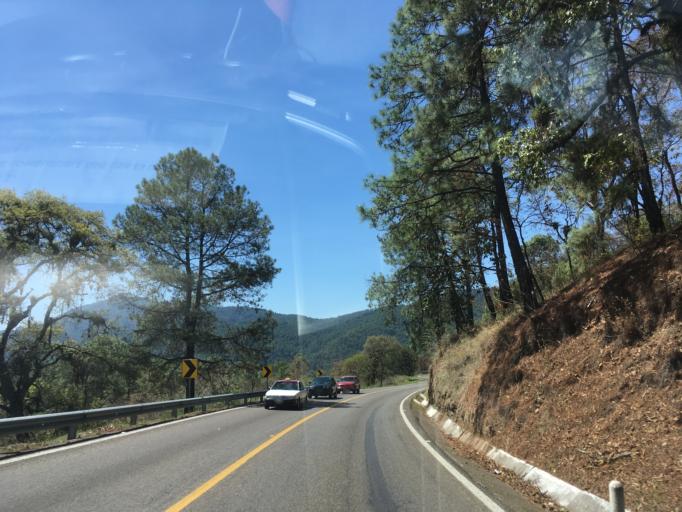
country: MX
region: Michoacan
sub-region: Hidalgo
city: Tierras Coloradas (San Pedro)
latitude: 19.6697
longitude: -100.7216
